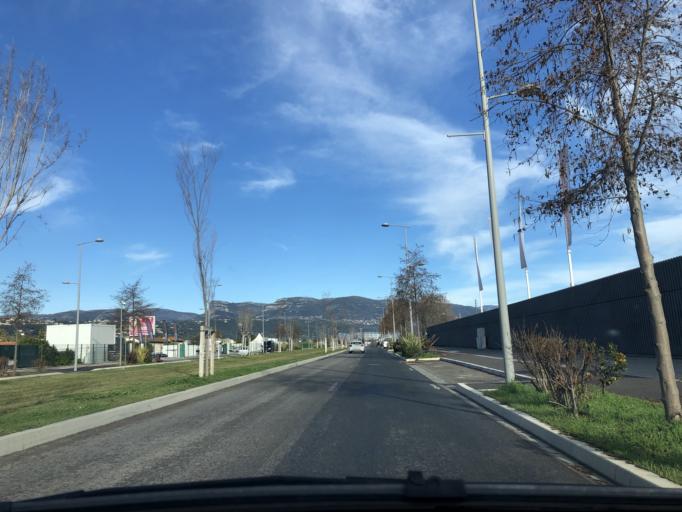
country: FR
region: Provence-Alpes-Cote d'Azur
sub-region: Departement des Alpes-Maritimes
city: Saint-Laurent-du-Var
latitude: 43.6907
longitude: 7.2005
